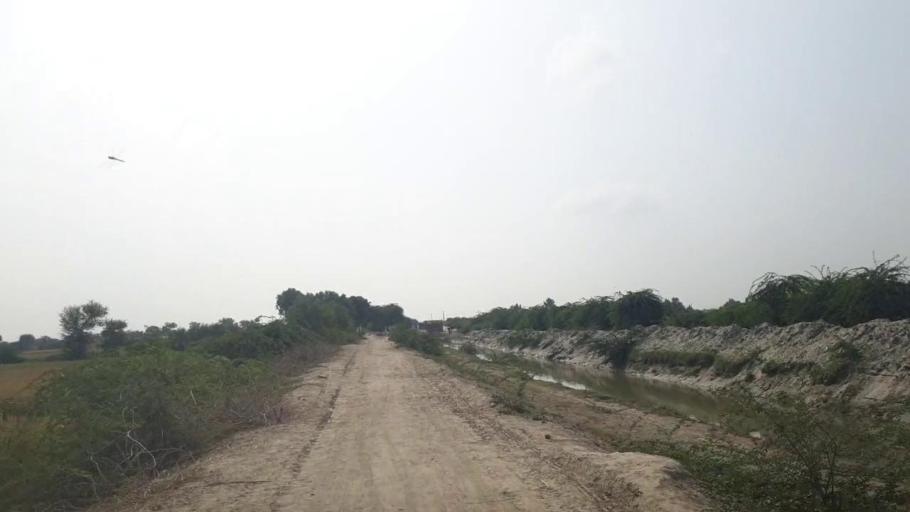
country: PK
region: Sindh
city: Badin
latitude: 24.6010
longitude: 68.7187
